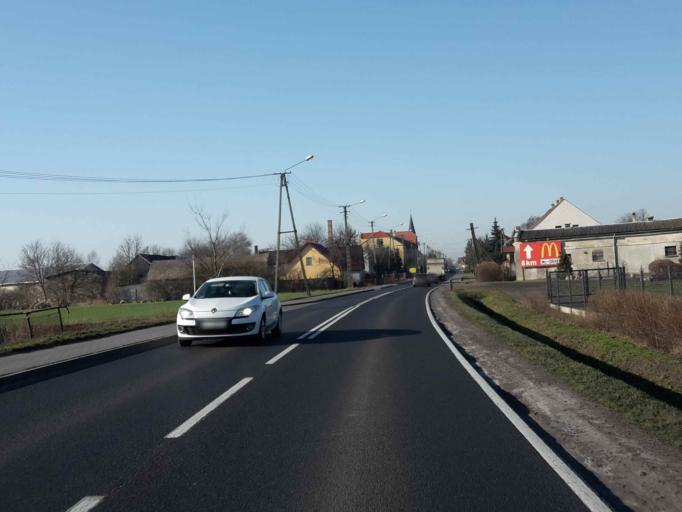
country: PL
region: Kujawsko-Pomorskie
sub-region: Powiat inowroclawski
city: Wierzchoslawice
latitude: 52.8484
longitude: 18.3411
